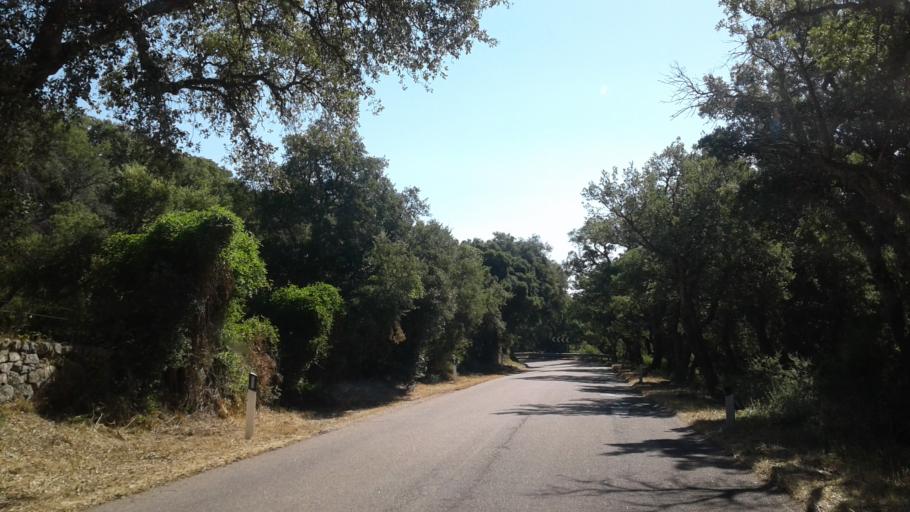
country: IT
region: Sardinia
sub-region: Provincia di Olbia-Tempio
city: Aggius
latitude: 40.9386
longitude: 9.0805
